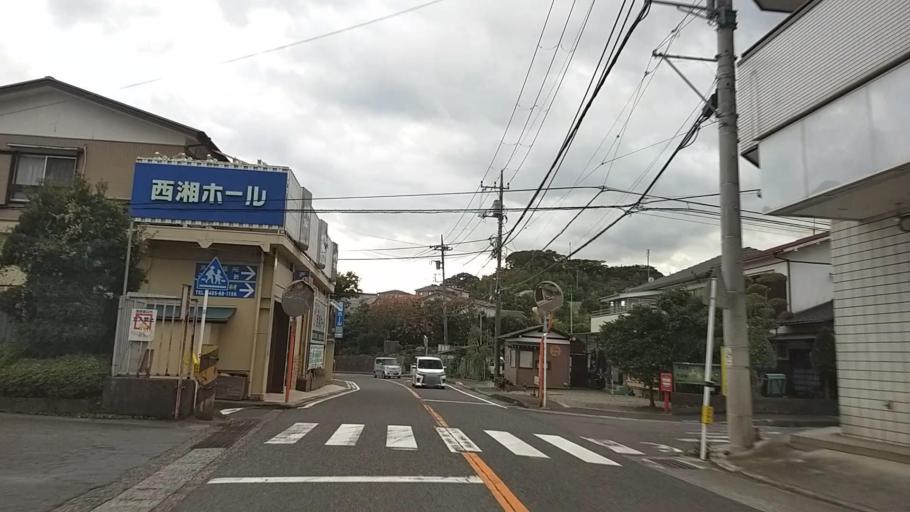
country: JP
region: Kanagawa
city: Yugawara
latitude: 35.1600
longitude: 139.1314
